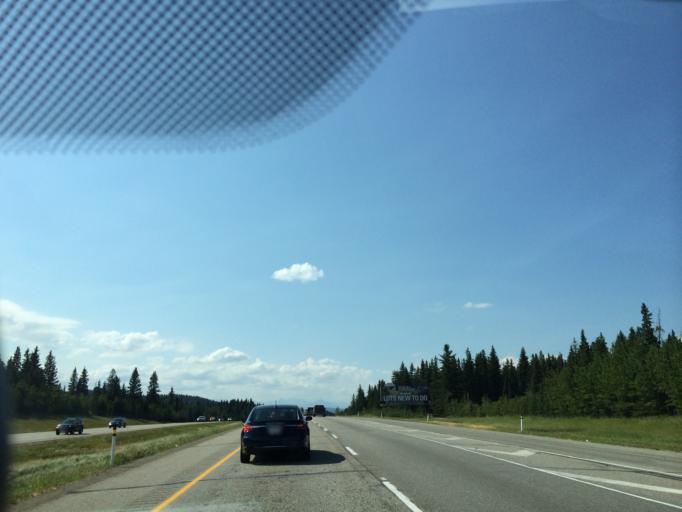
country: CA
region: Alberta
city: Cochrane
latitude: 51.1452
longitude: -114.7289
